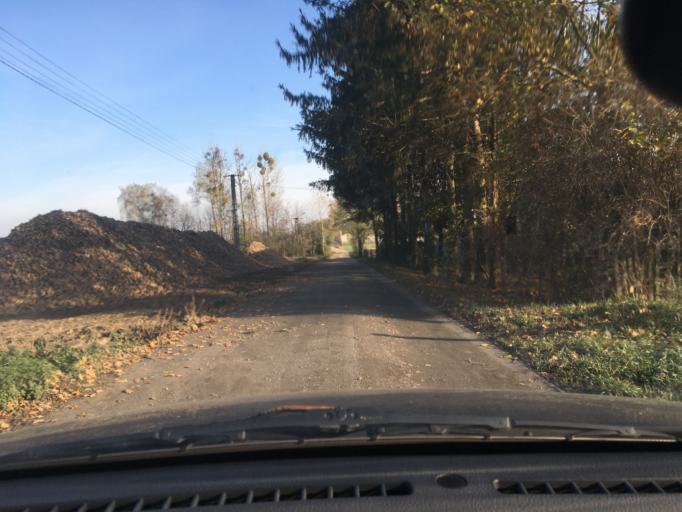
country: PL
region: Masovian Voivodeship
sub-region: Powiat plocki
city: Mala Wies
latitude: 52.4433
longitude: 20.1060
